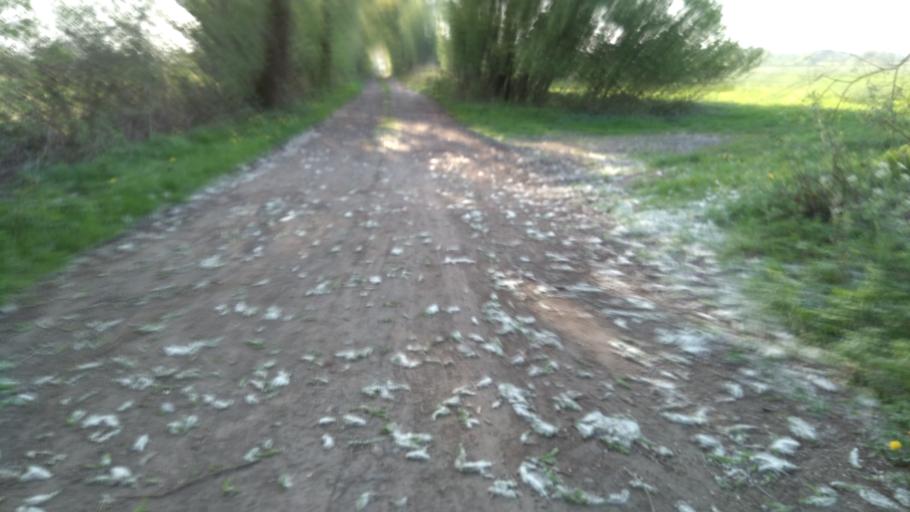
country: DE
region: Lower Saxony
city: Apensen
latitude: 53.4378
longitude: 9.5764
